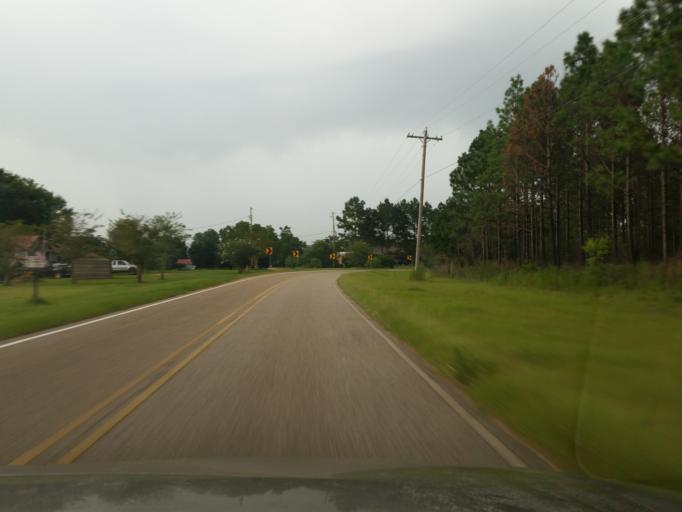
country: US
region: Alabama
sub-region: Baldwin County
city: Robertsdale
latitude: 30.5835
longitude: -87.5709
